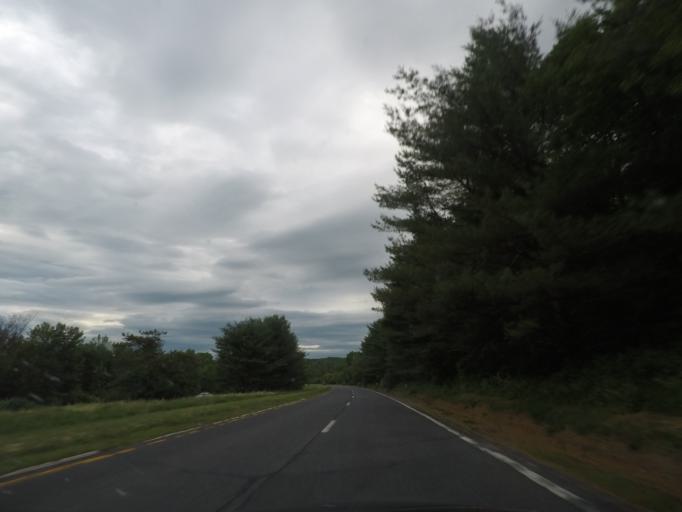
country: US
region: New York
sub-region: Dutchess County
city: Pine Plains
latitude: 41.9883
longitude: -73.7355
